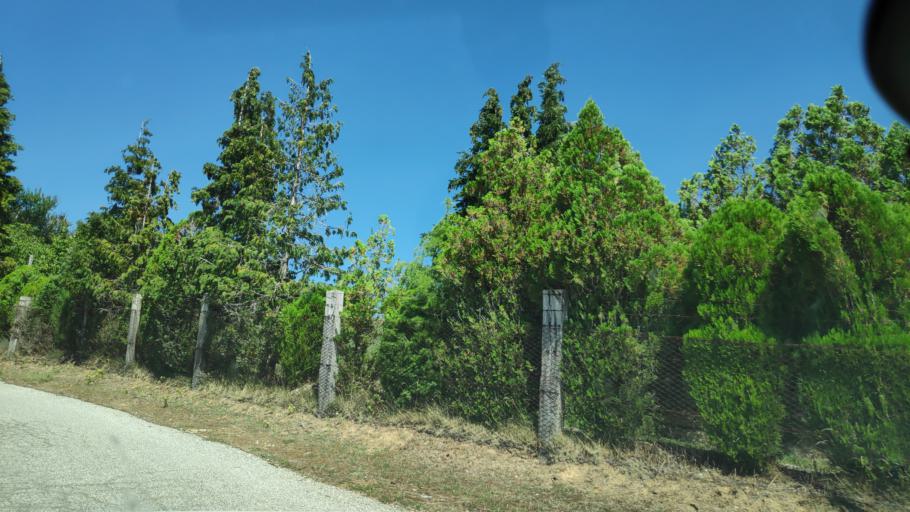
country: IT
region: Calabria
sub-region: Provincia di Reggio Calabria
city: Bova
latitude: 38.0255
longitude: 15.9432
